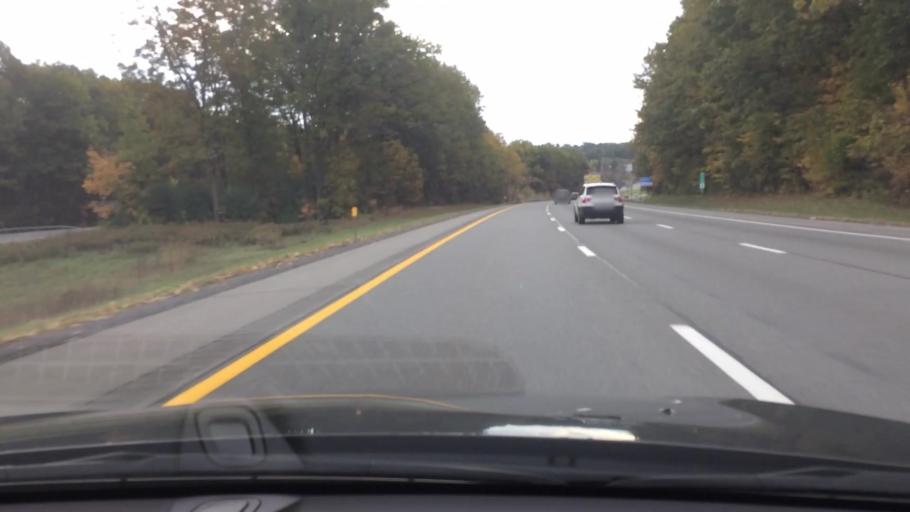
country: US
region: New York
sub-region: Saratoga County
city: Country Knolls
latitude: 42.8973
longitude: -73.7824
